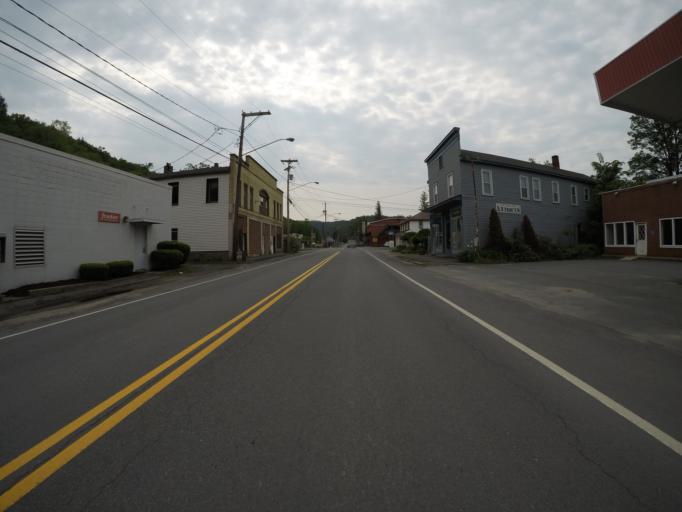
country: US
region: New York
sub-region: Sullivan County
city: Livingston Manor
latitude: 41.9337
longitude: -74.9140
